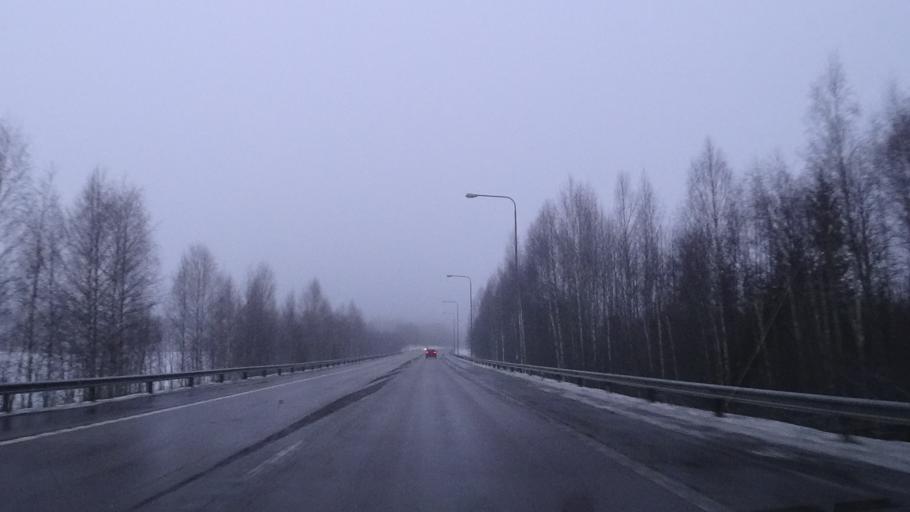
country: FI
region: Paijanne Tavastia
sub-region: Lahti
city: Hollola
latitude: 60.9835
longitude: 25.4400
